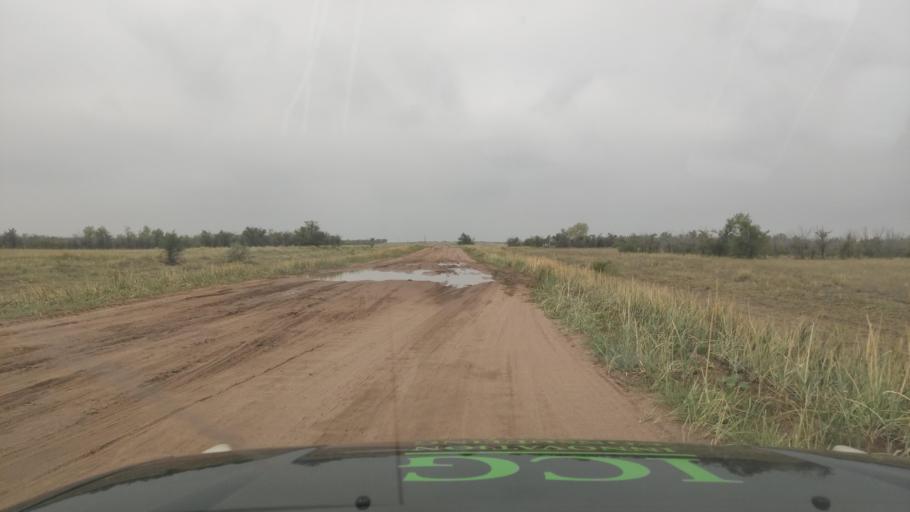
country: KZ
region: Pavlodar
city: Aksu
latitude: 52.0618
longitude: 77.1596
